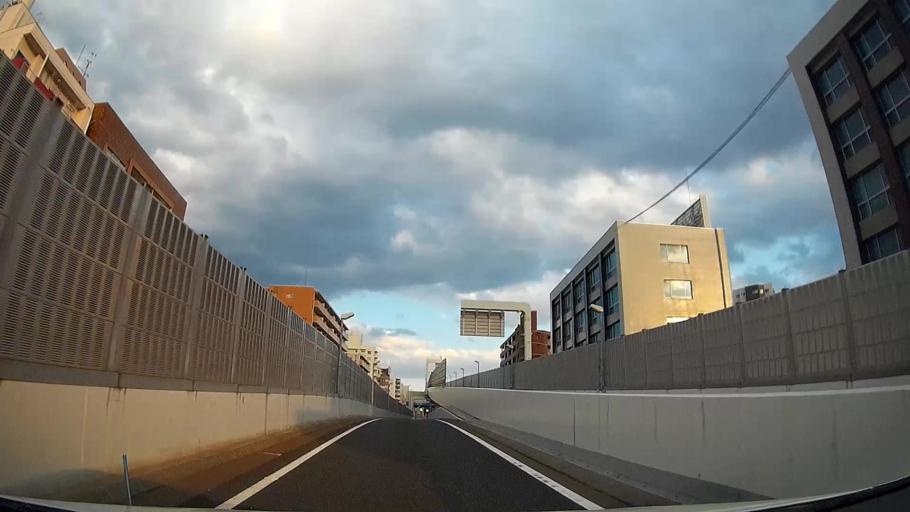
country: JP
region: Saitama
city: Kawaguchi
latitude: 35.7580
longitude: 139.7390
